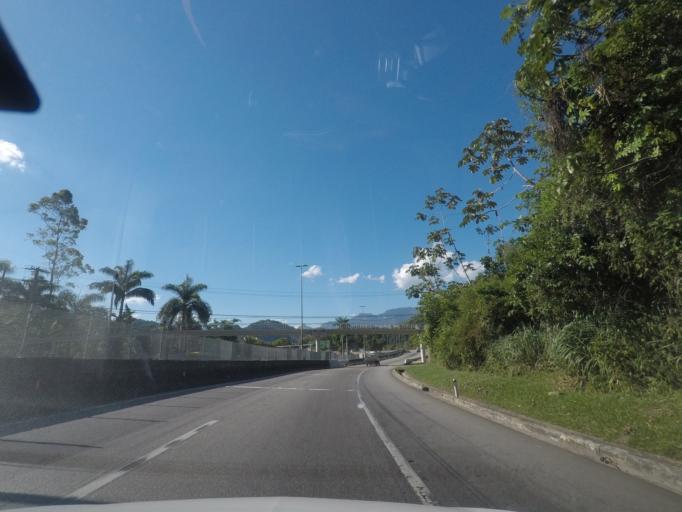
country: BR
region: Rio de Janeiro
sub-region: Petropolis
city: Petropolis
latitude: -22.6624
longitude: -43.1162
